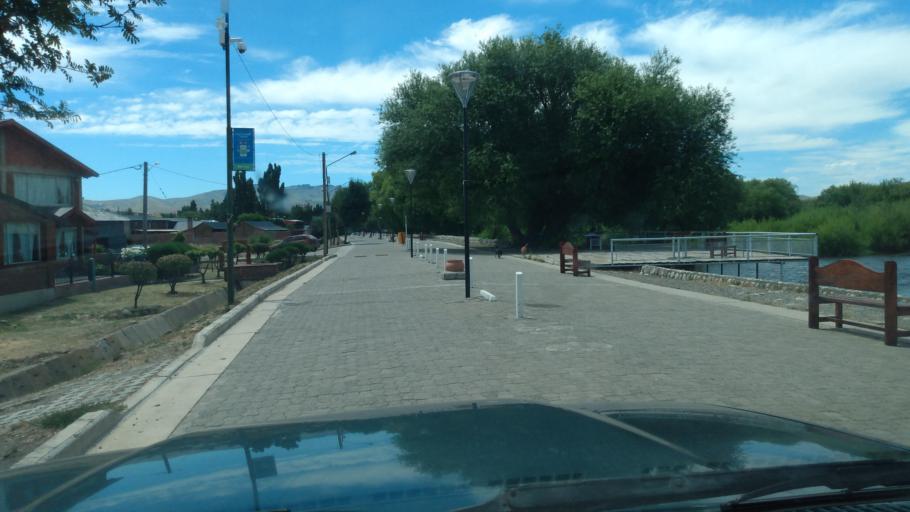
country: AR
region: Neuquen
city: Junin de los Andes
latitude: -39.9498
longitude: -71.0646
